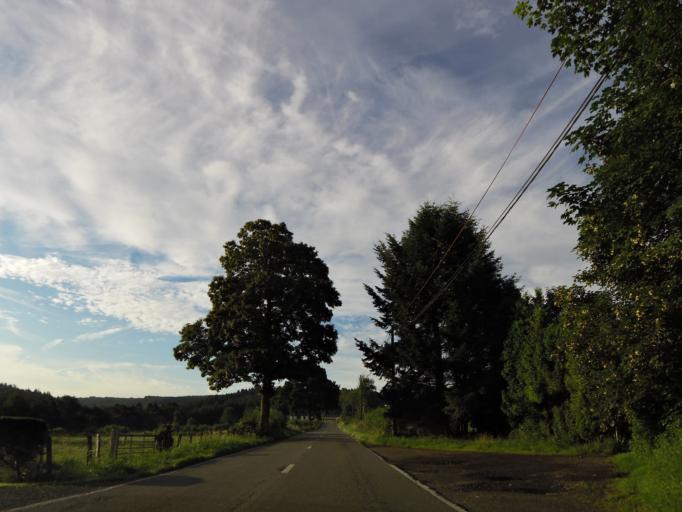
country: BE
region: Wallonia
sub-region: Province de Liege
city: Jalhay
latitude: 50.5097
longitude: 5.9534
